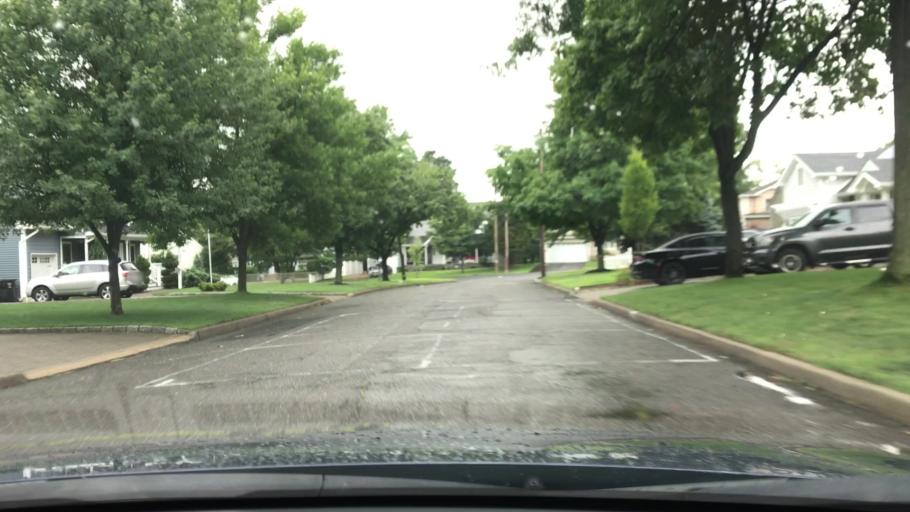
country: US
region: New Jersey
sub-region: Bergen County
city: Paramus
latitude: 40.9685
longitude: -74.0890
